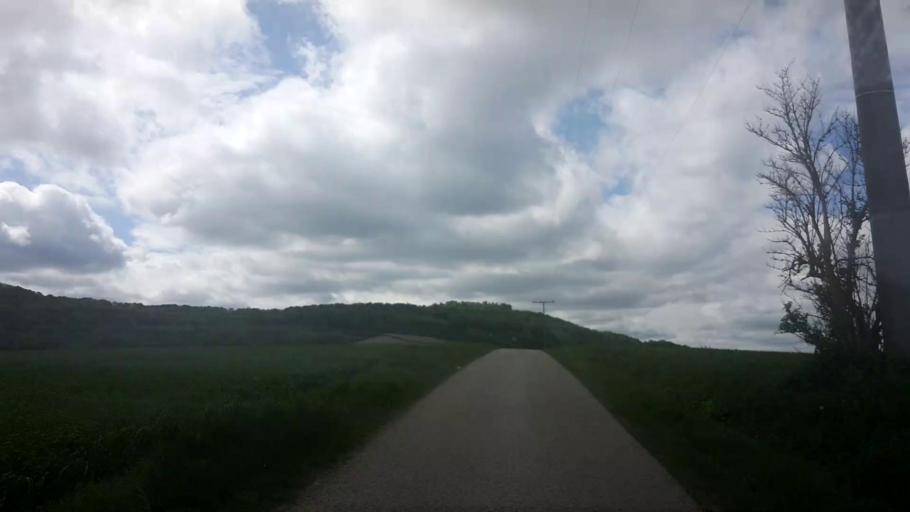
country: DE
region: Bavaria
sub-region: Upper Franconia
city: Bad Staffelstein
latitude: 50.1043
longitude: 11.0353
